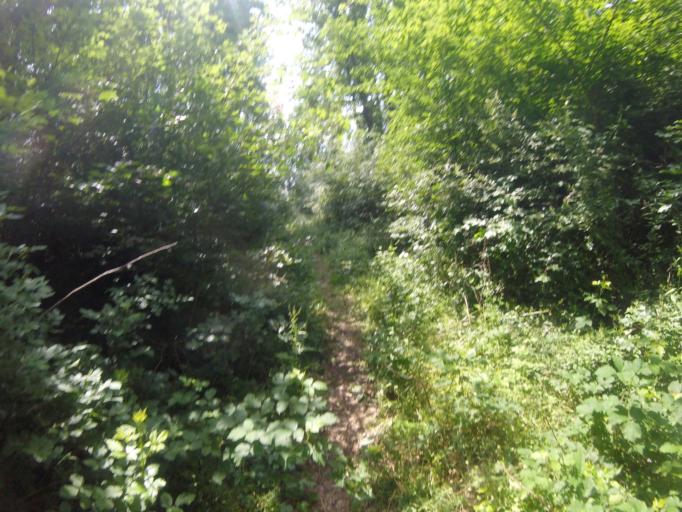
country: HU
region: Zala
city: Cserszegtomaj
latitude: 46.9051
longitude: 17.1934
